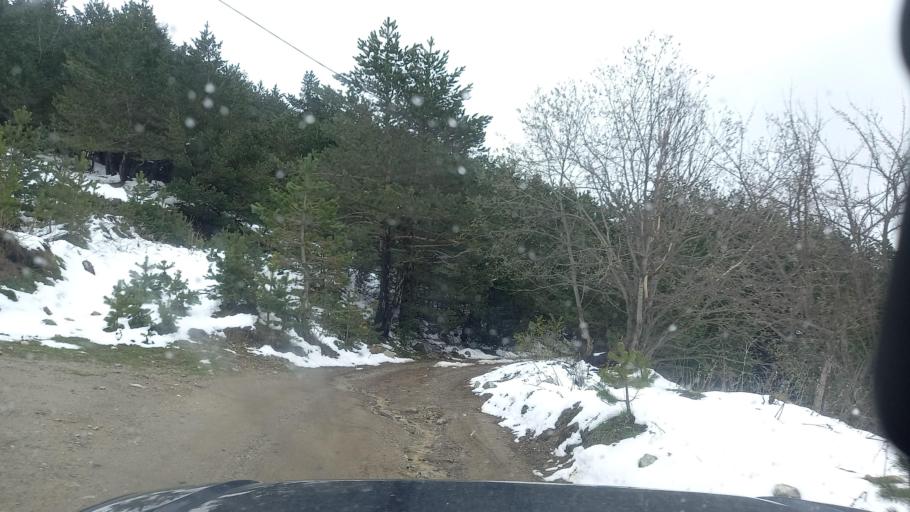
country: RU
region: North Ossetia
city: Mizur
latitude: 42.8087
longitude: 43.9592
